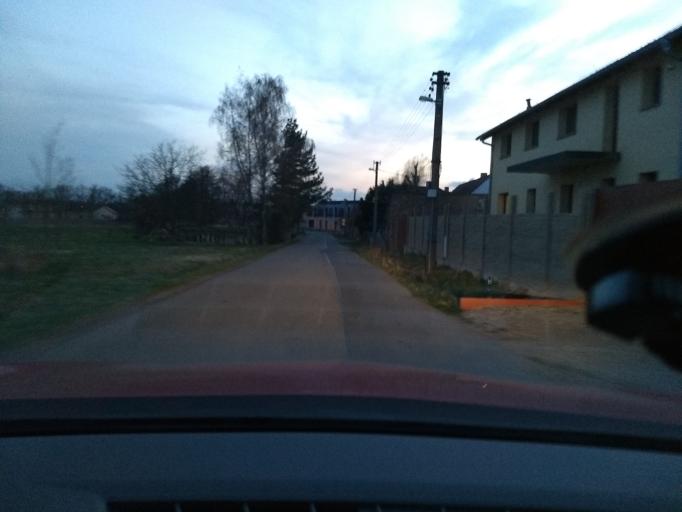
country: CZ
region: Central Bohemia
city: Jenec
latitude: 50.0522
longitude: 14.1829
